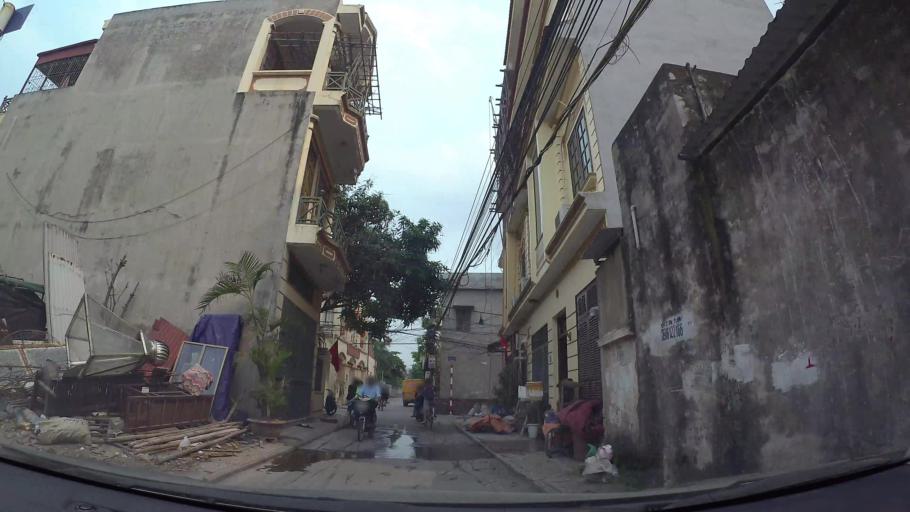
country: VN
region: Ha Noi
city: Trau Quy
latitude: 21.0589
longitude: 105.8999
